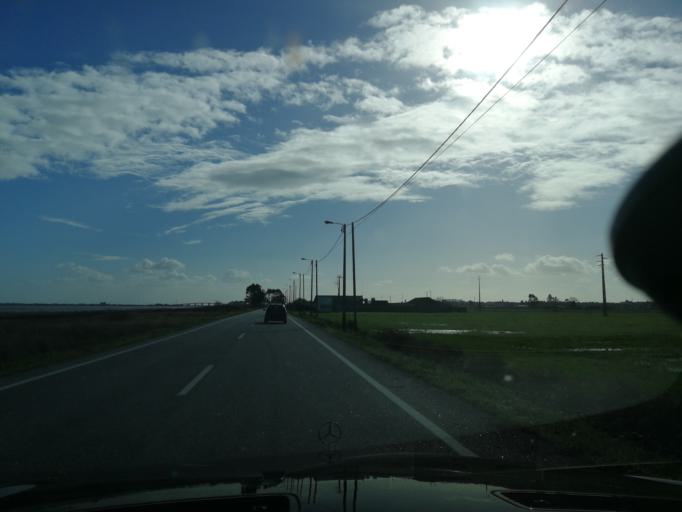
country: PT
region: Aveiro
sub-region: Estarreja
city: Pardilho
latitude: 40.8096
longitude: -8.6717
